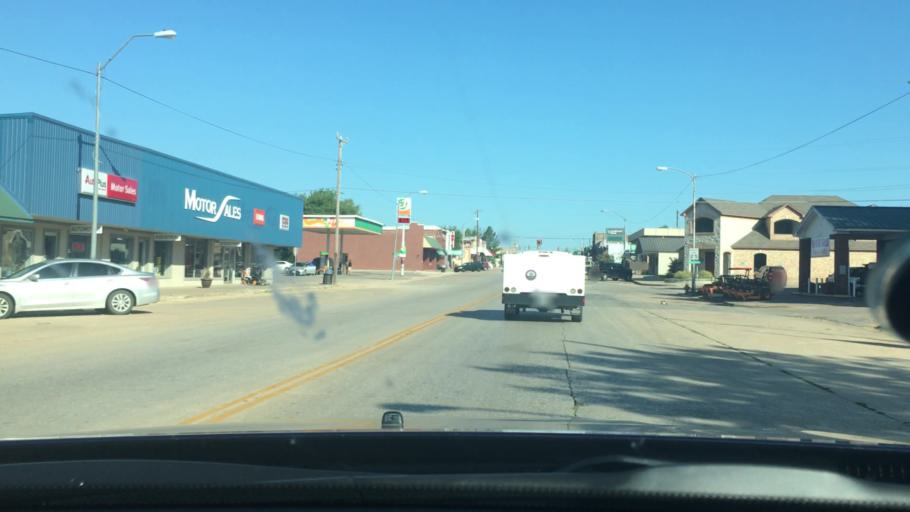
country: US
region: Oklahoma
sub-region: Johnston County
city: Tishomingo
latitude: 34.2344
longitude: -96.6766
